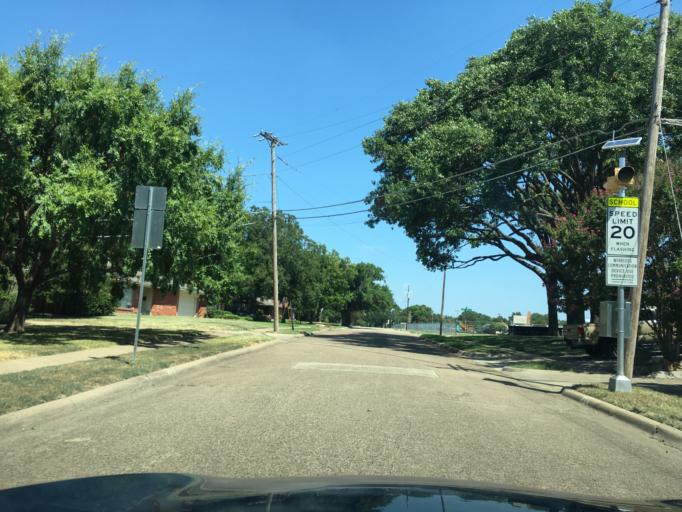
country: US
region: Texas
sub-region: Dallas County
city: Garland
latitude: 32.8528
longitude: -96.6887
